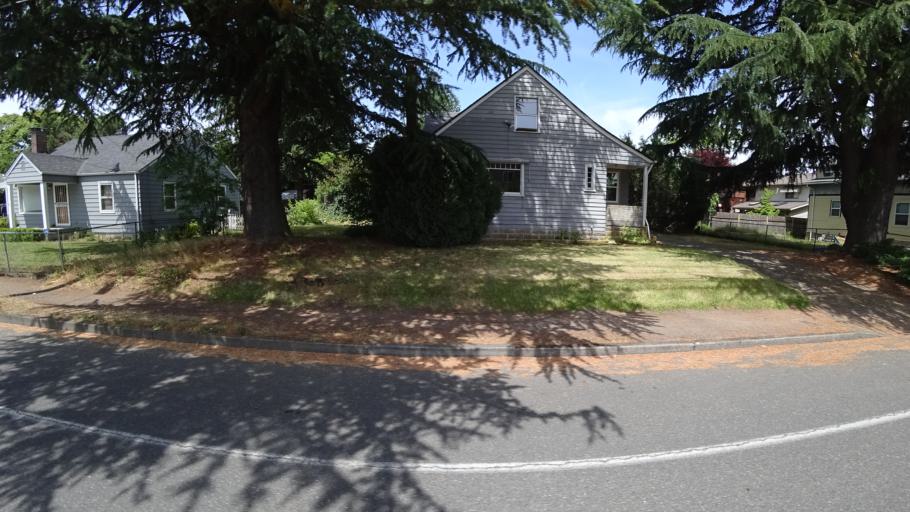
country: US
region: Oregon
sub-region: Multnomah County
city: Lents
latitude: 45.4687
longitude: -122.5987
